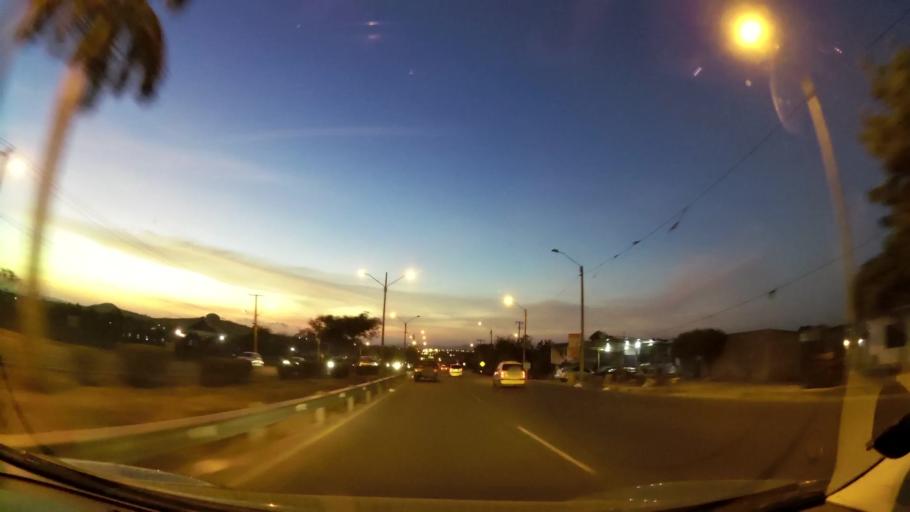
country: CO
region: Atlantico
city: Soledad
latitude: 10.9239
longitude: -74.8189
